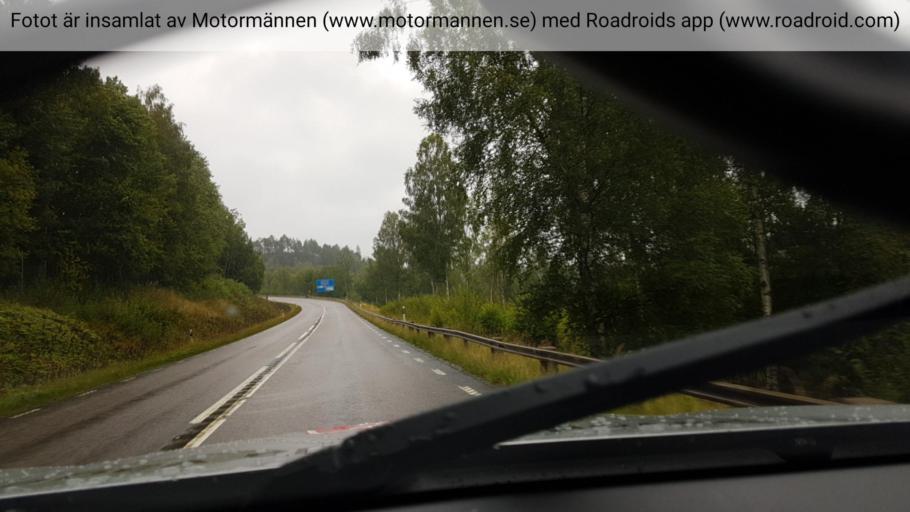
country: SE
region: Vaestra Goetaland
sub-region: Bengtsfors Kommun
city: Billingsfors
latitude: 59.0118
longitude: 12.2725
